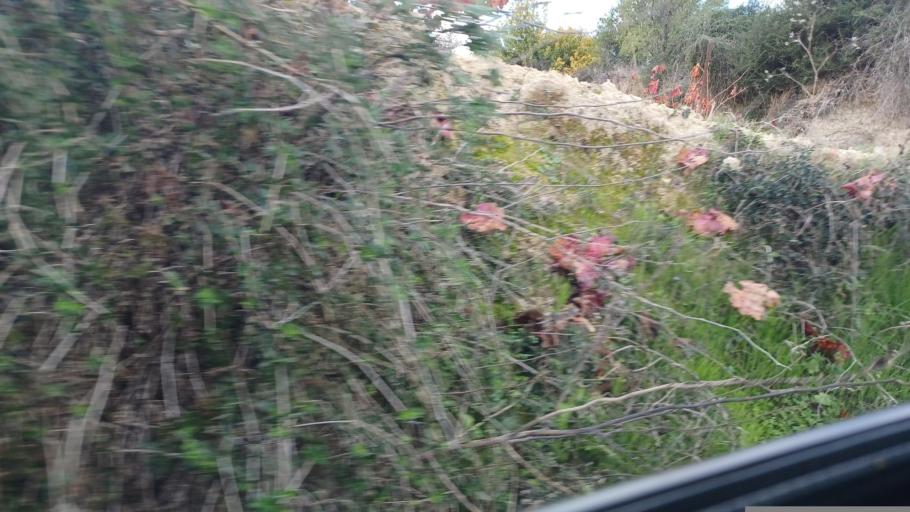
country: CY
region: Pafos
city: Mesogi
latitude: 34.8360
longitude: 32.5265
